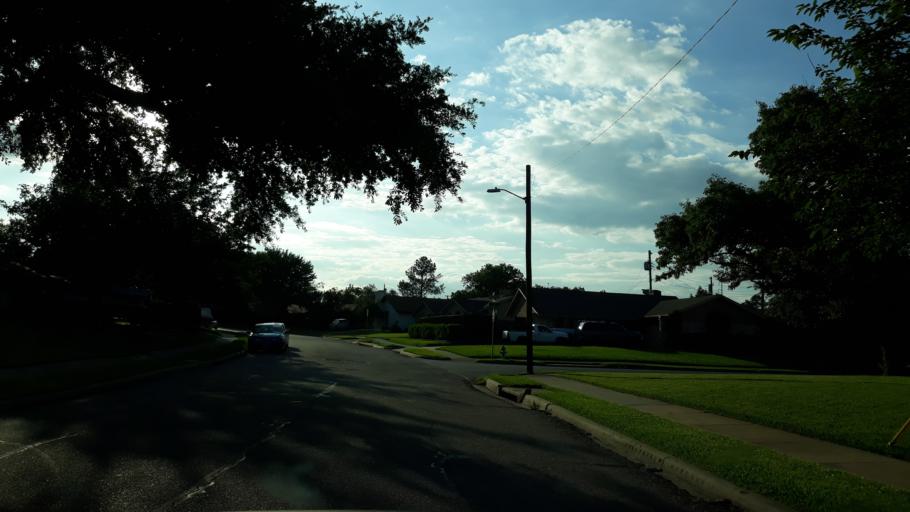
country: US
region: Texas
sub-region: Dallas County
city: Irving
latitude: 32.8544
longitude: -96.9986
